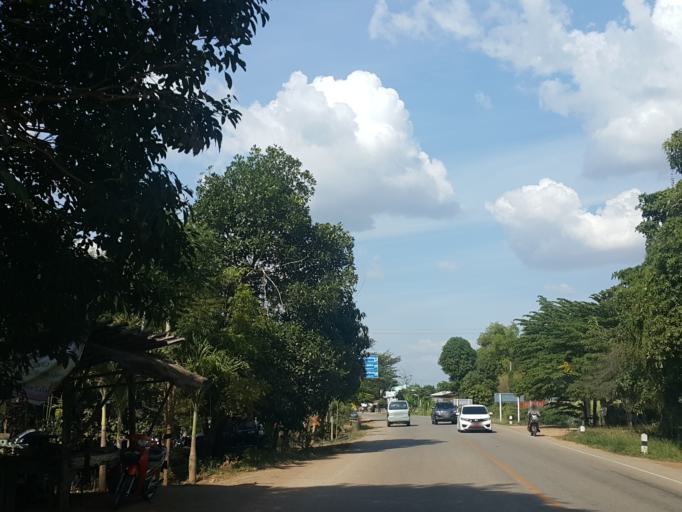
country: TH
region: Sukhothai
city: Sawankhalok
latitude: 17.2978
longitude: 99.8265
